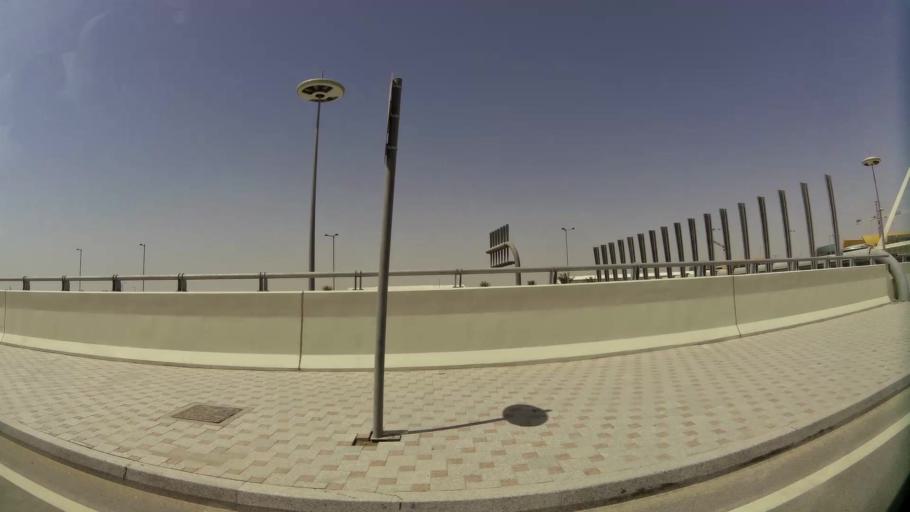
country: QA
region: Baladiyat Umm Salal
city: Umm Salal Muhammad
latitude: 25.3987
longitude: 51.5154
